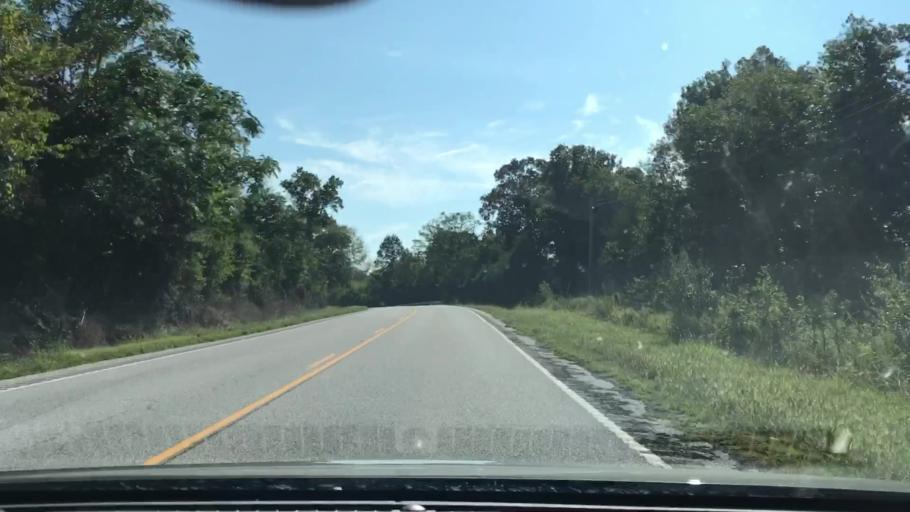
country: US
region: Tennessee
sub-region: Jackson County
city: Gainesboro
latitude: 36.3587
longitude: -85.7432
